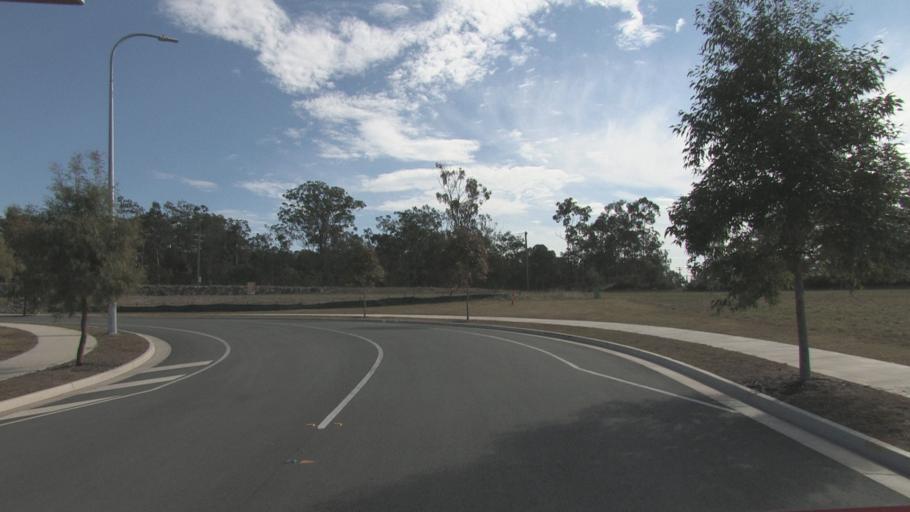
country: AU
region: Queensland
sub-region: Logan
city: Chambers Flat
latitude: -27.8019
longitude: 153.1006
